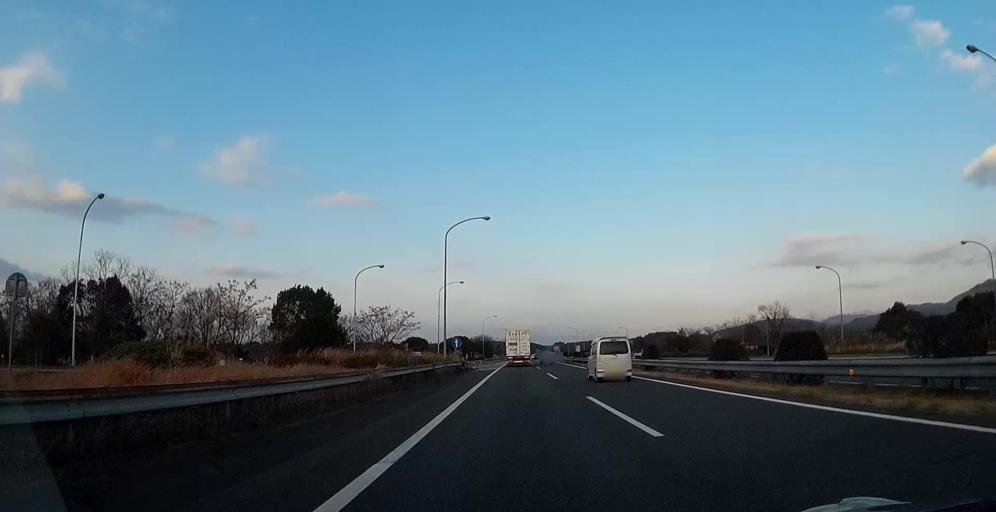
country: JP
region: Kumamoto
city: Kumamoto
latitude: 32.7334
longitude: 130.7767
